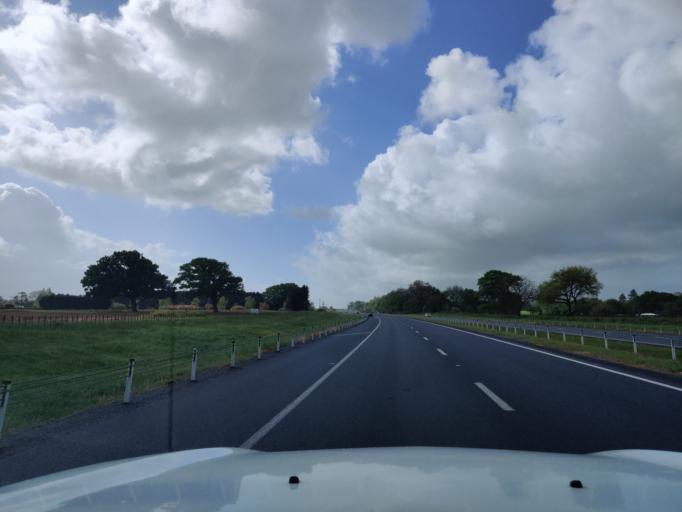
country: NZ
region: Waikato
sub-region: Waipa District
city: Cambridge
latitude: -37.8403
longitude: 175.3693
